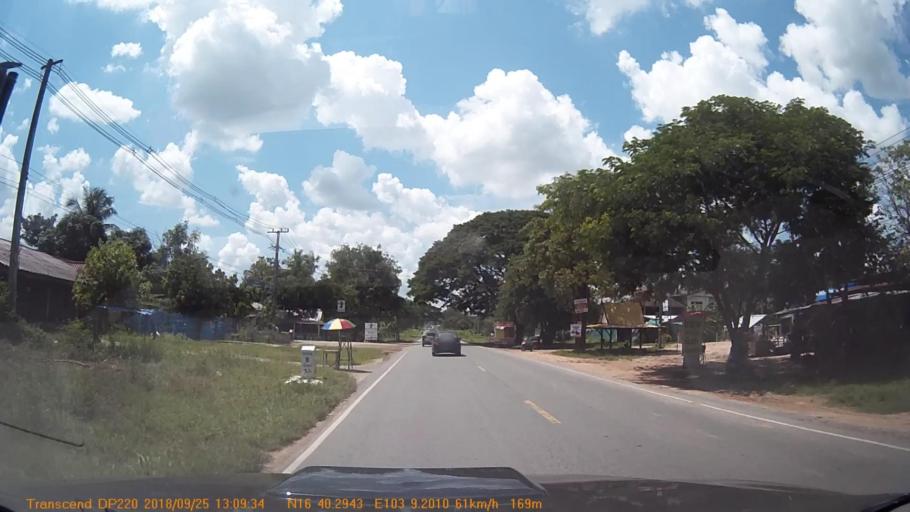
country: TH
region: Khon Kaen
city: Kranuan
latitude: 16.6716
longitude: 103.1534
